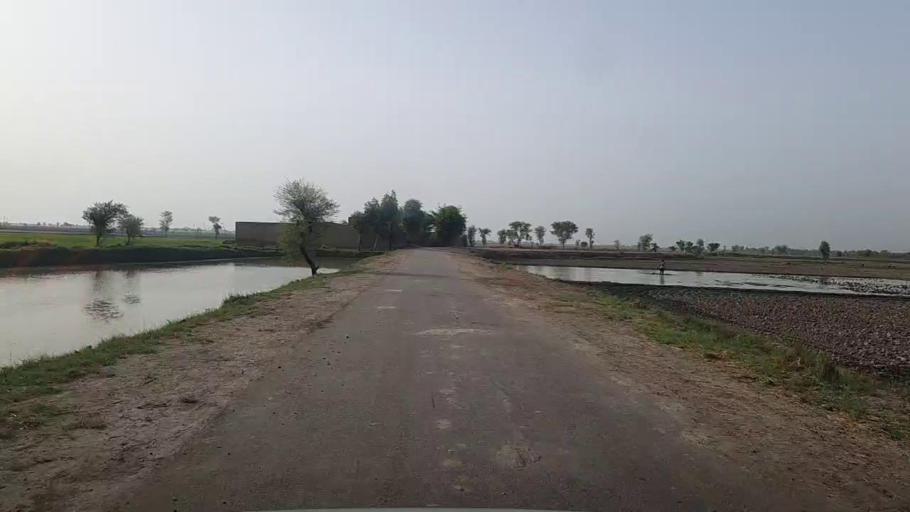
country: PK
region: Sindh
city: Khairpur Nathan Shah
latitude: 27.0970
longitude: 67.7944
